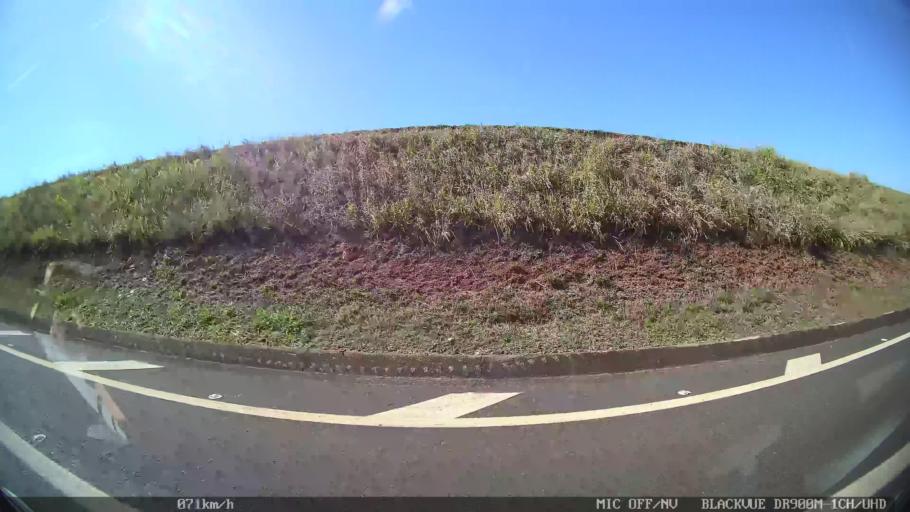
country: BR
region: Sao Paulo
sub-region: Franca
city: Franca
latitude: -20.6810
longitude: -47.4960
